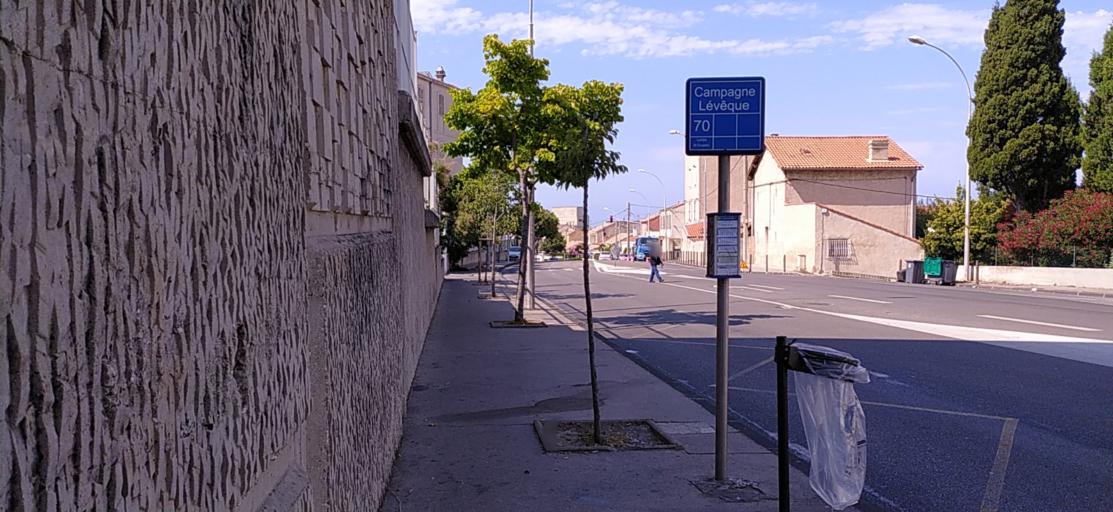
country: FR
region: Provence-Alpes-Cote d'Azur
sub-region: Departement des Bouches-du-Rhone
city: Marseille 16
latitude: 43.3426
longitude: 5.3529
